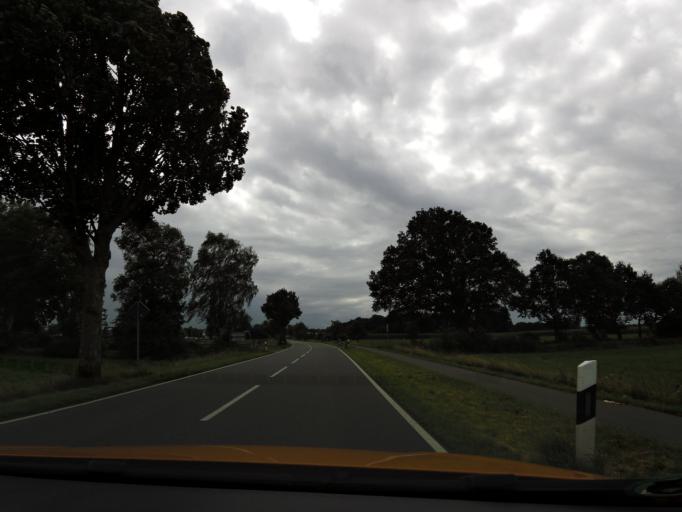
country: DE
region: Lower Saxony
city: Gross Ippener
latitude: 52.9805
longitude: 8.6152
